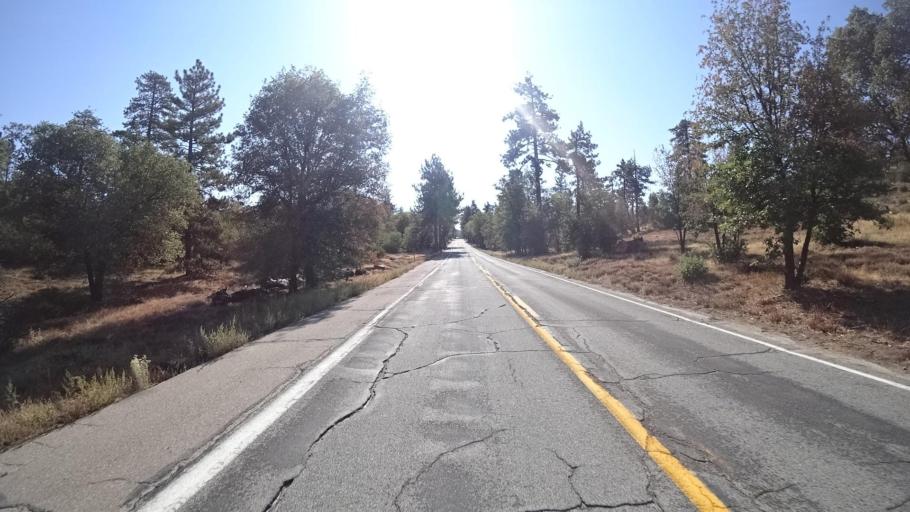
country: US
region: California
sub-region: San Diego County
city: Pine Valley
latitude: 32.8866
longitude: -116.4342
